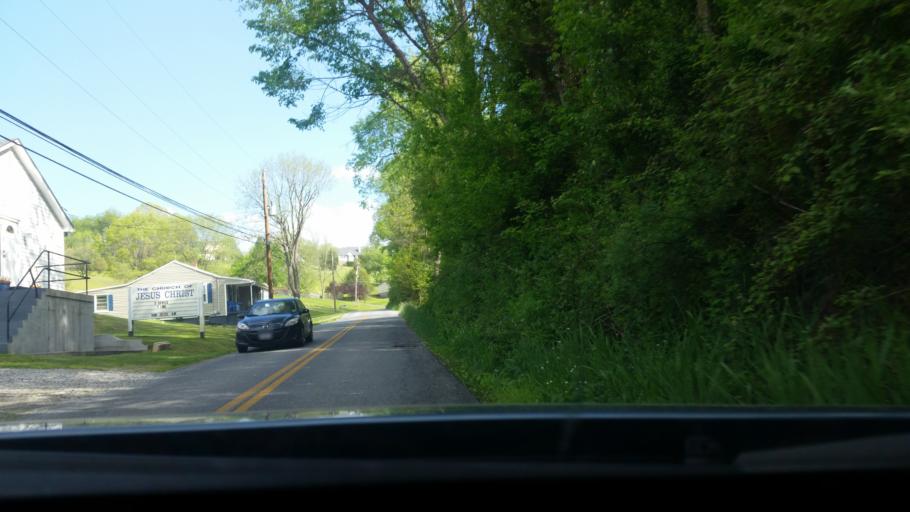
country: US
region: Virginia
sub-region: Giles County
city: Pembroke
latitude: 37.3145
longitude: -80.6327
